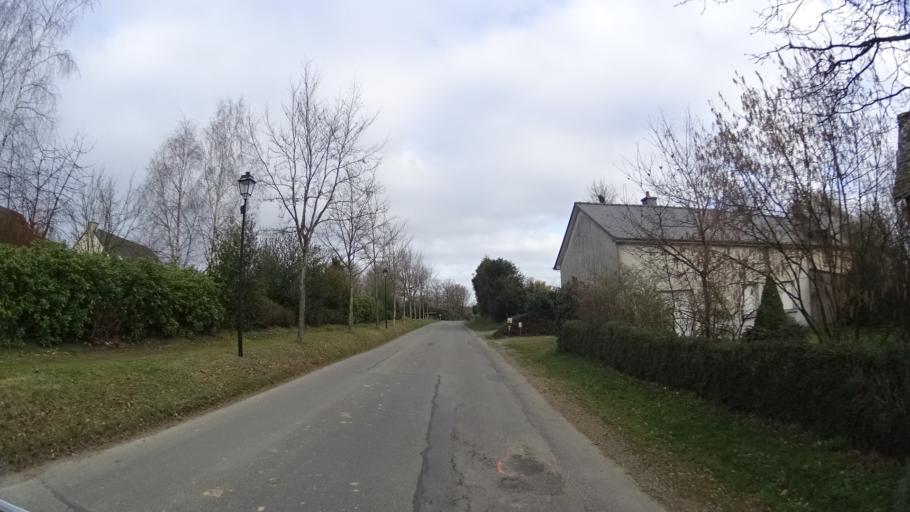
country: FR
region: Brittany
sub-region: Departement d'Ille-et-Vilaine
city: Saint-Gilles
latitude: 48.1806
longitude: -1.8532
